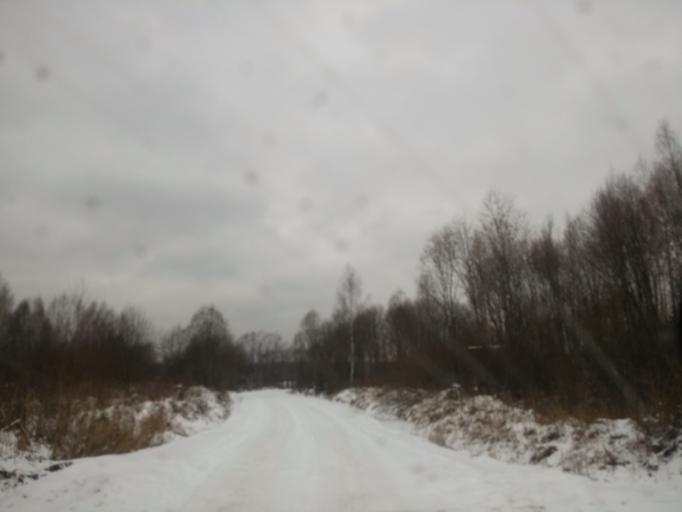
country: RU
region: Moskovskaya
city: Reshetnikovo
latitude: 56.4591
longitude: 36.5453
